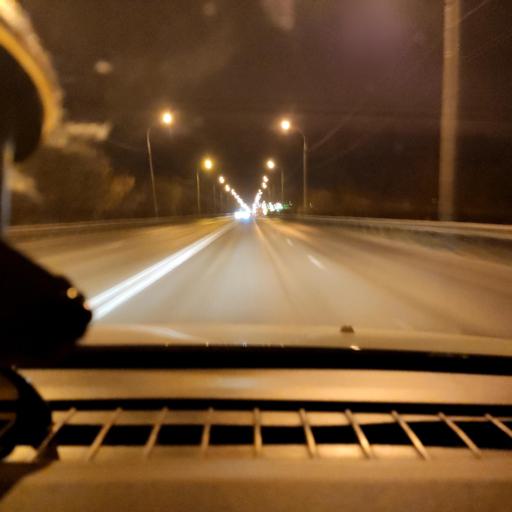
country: RU
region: Samara
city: Samara
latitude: 53.1486
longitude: 50.1848
